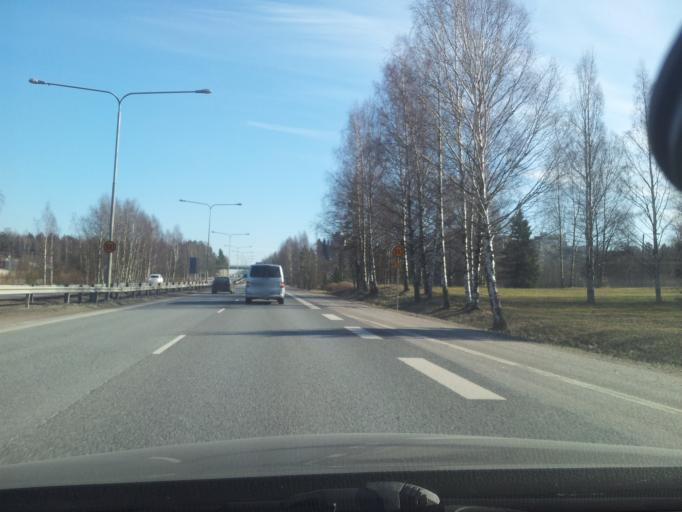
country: FI
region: Uusimaa
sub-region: Helsinki
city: Espoo
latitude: 60.1567
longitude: 24.6364
